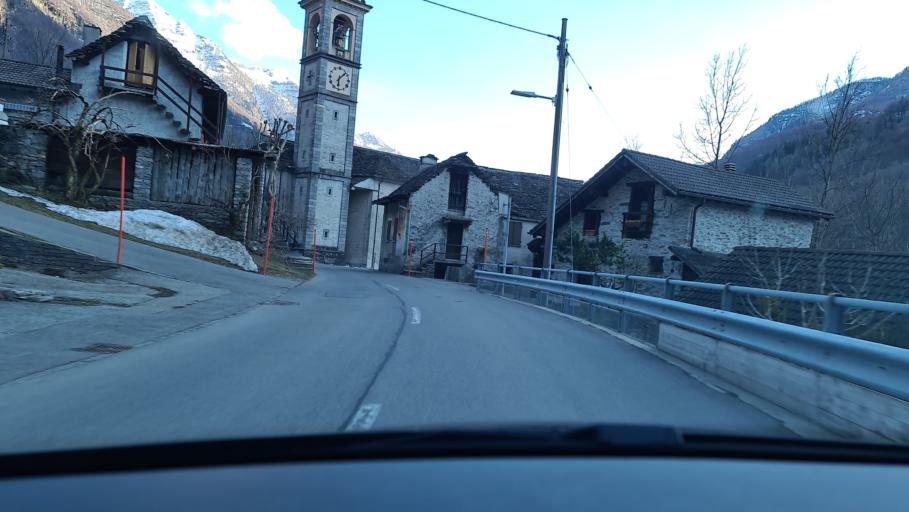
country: CH
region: Ticino
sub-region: Locarno District
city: Lavertezzo
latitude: 46.3407
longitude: 8.8018
